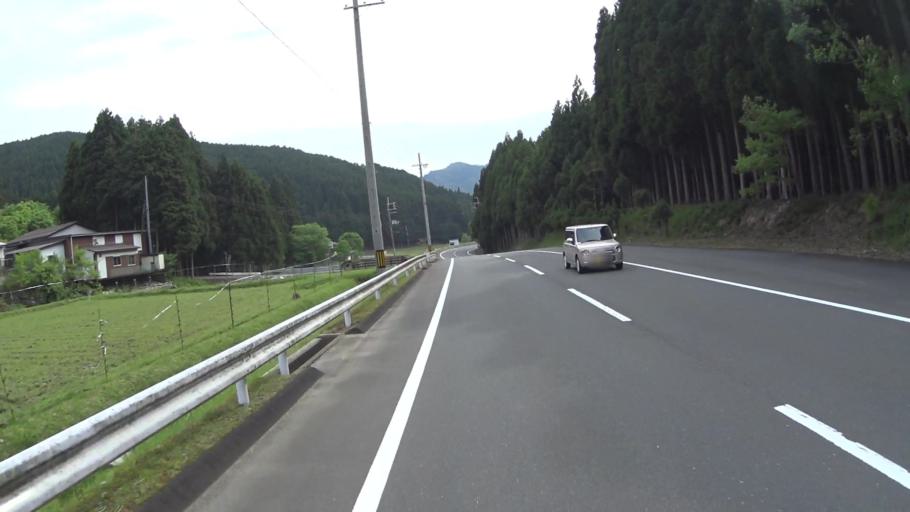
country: JP
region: Kyoto
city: Kameoka
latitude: 35.1451
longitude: 135.6166
